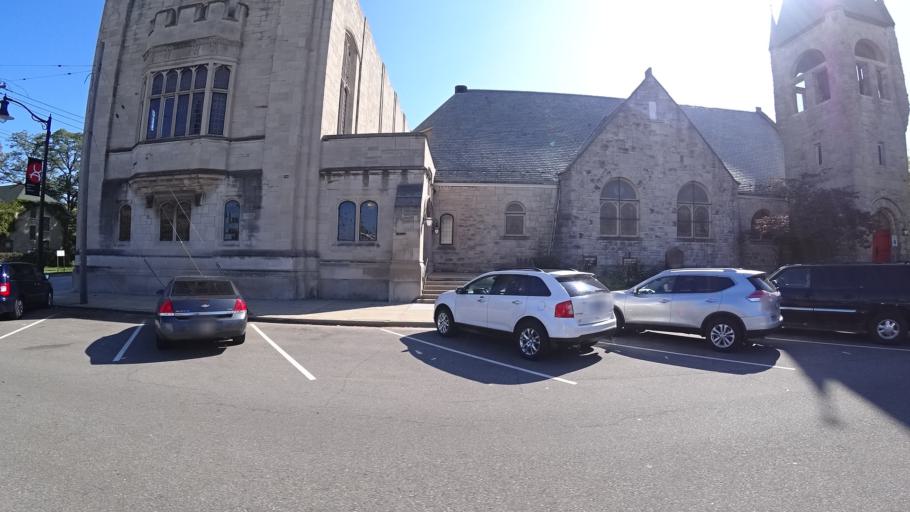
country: US
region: Indiana
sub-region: LaPorte County
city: Michigan City
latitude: 41.7163
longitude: -86.9008
